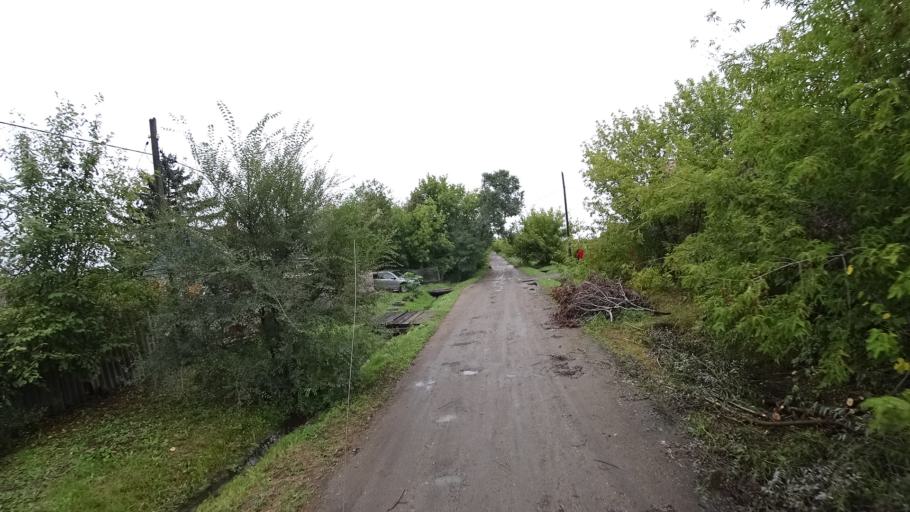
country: RU
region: Primorskiy
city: Monastyrishche
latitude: 44.2124
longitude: 132.4290
